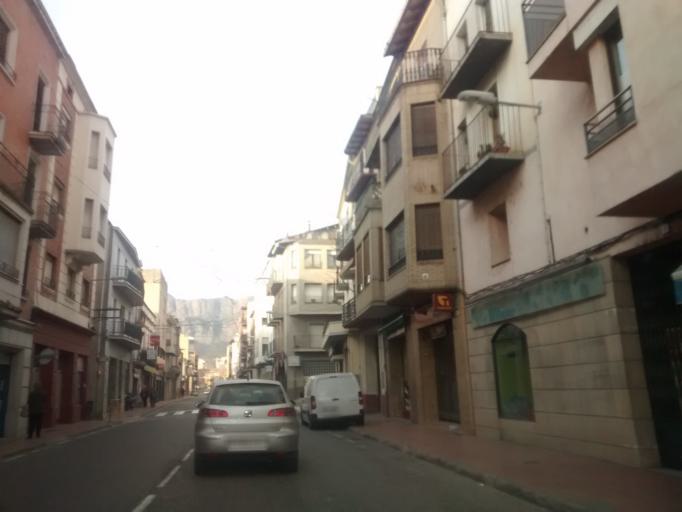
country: ES
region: Catalonia
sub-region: Provincia de Lleida
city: Oliana
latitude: 42.0670
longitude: 1.3138
